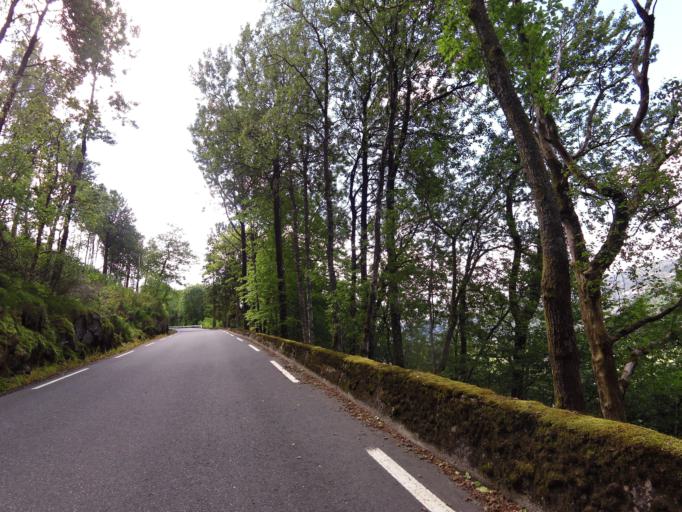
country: NO
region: Vest-Agder
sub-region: Kvinesdal
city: Liknes
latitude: 58.2911
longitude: 6.9401
